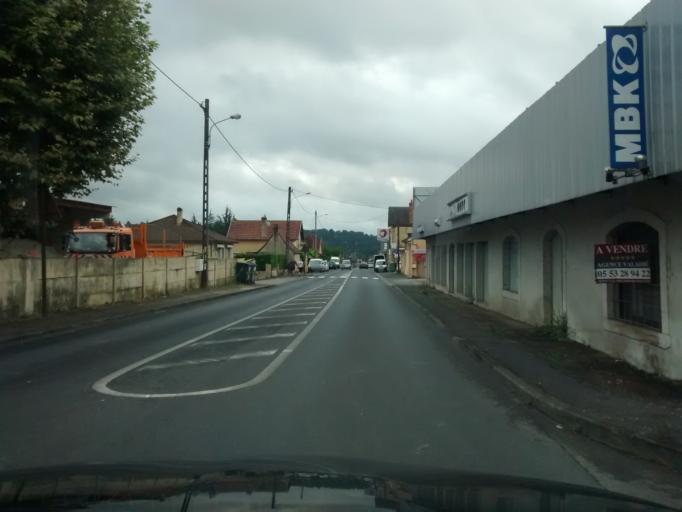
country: FR
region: Aquitaine
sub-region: Departement de la Dordogne
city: Sarlat-la-Caneda
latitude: 44.9009
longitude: 1.2112
